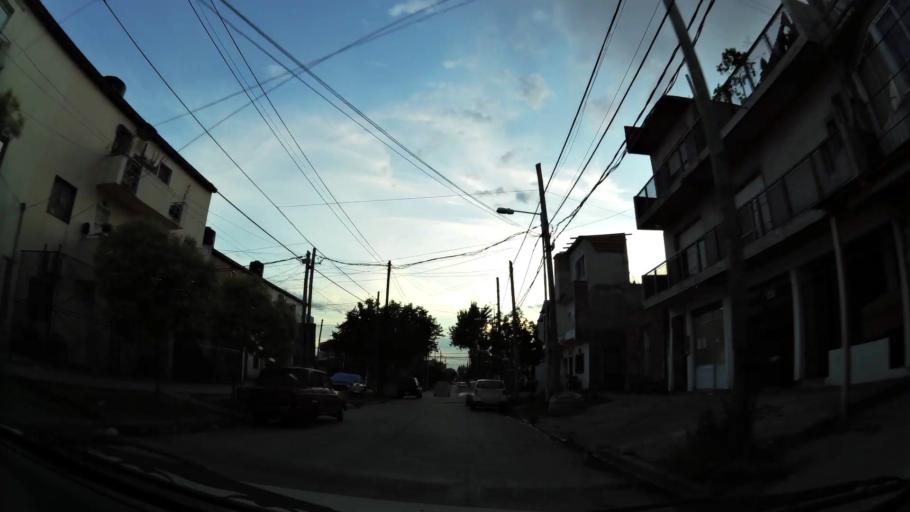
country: AR
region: Buenos Aires
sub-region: Partido de Avellaneda
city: Avellaneda
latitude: -34.6840
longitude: -58.3302
